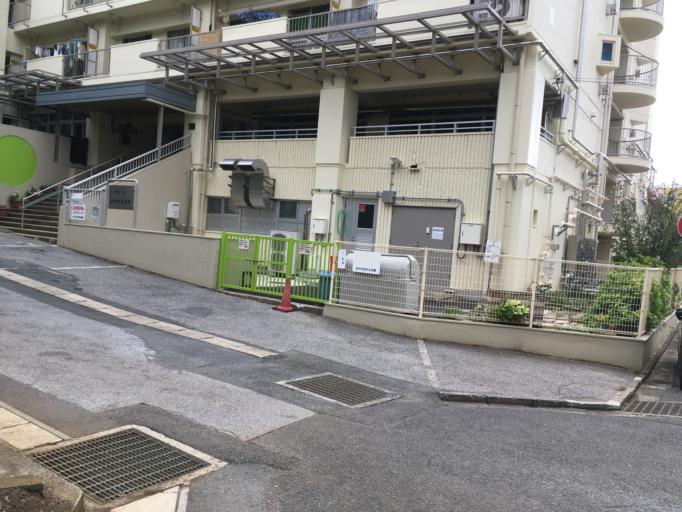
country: JP
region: Chiba
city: Kashiwa
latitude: 35.8225
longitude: 139.9376
